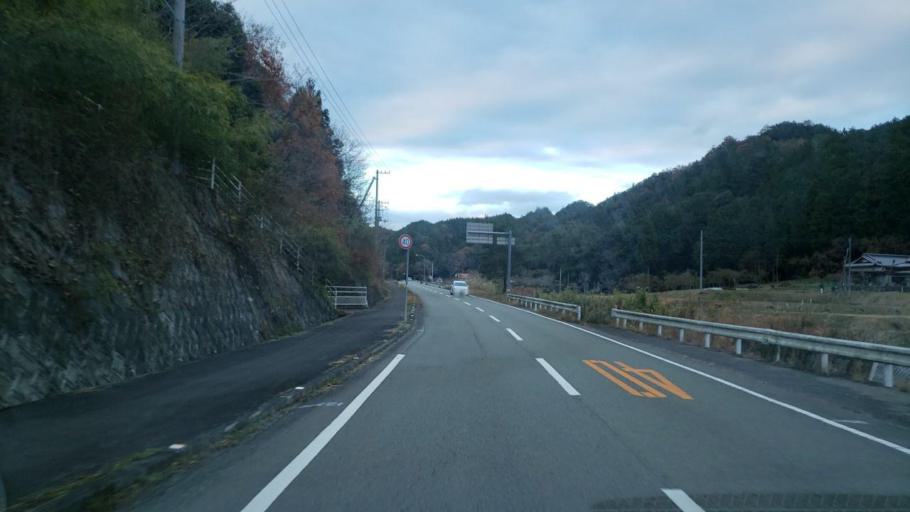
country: JP
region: Tokushima
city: Kamojimacho-jogejima
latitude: 34.1846
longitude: 134.2514
